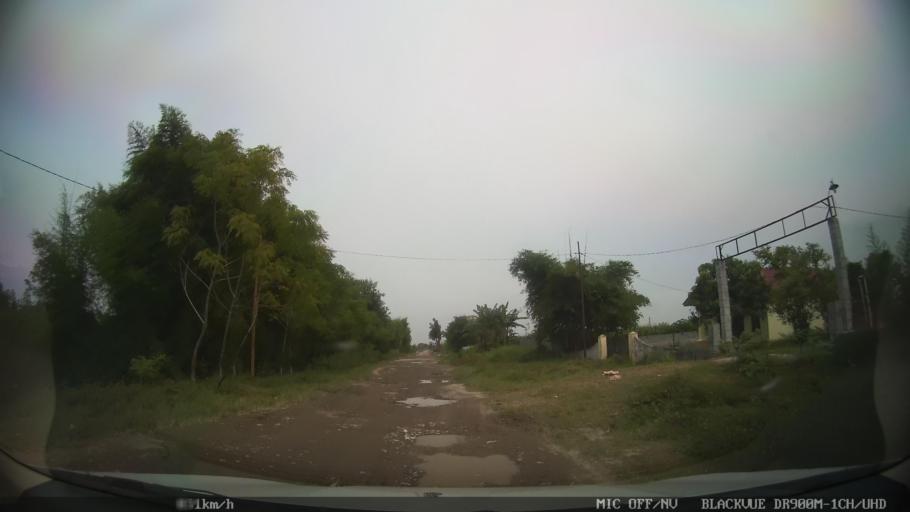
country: ID
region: North Sumatra
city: Medan
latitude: 3.5733
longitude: 98.7486
